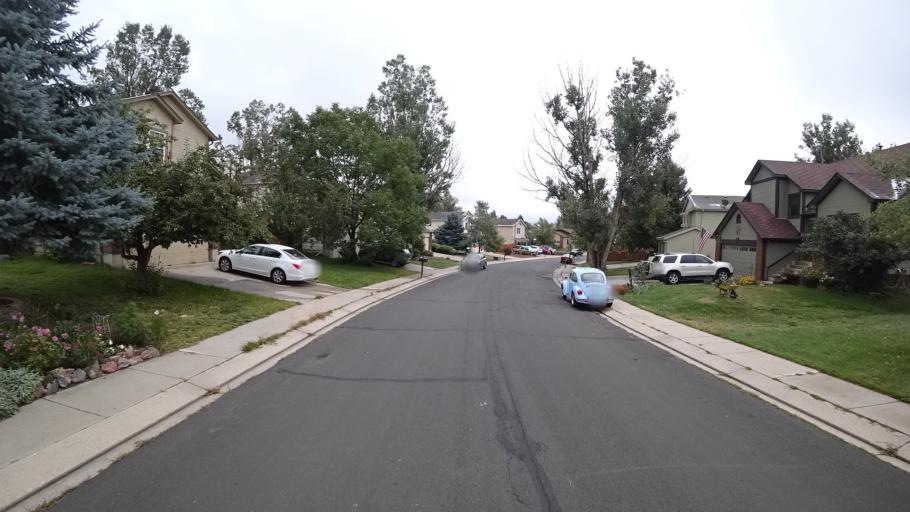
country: US
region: Colorado
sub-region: El Paso County
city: Cimarron Hills
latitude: 38.9203
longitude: -104.7574
